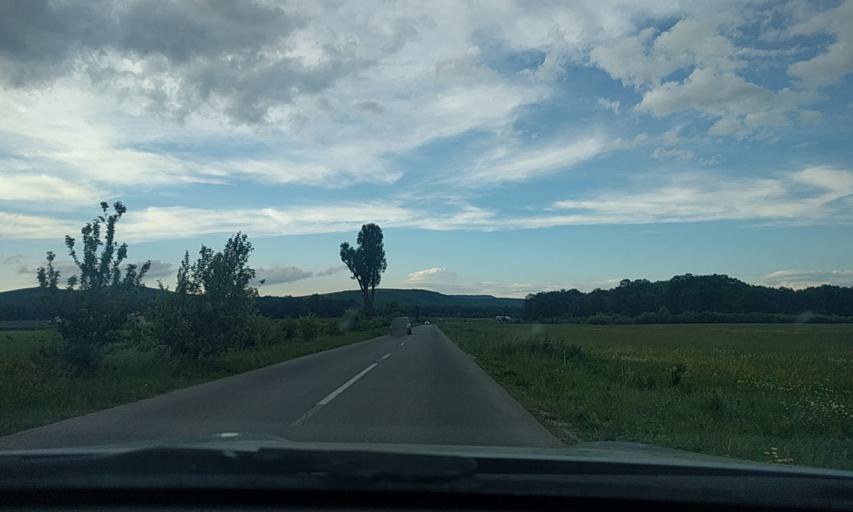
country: RO
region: Brasov
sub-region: Comuna Harman
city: Harman
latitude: 45.7422
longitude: 25.7040
